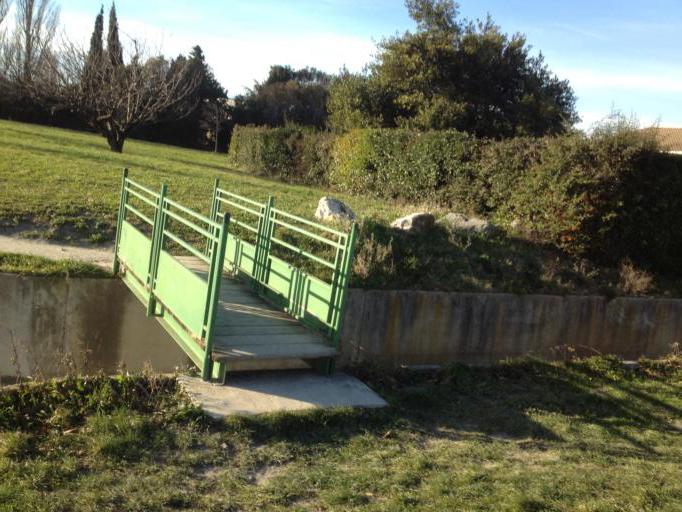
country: FR
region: Provence-Alpes-Cote d'Azur
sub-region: Departement du Vaucluse
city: Orange
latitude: 44.1261
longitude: 4.8370
